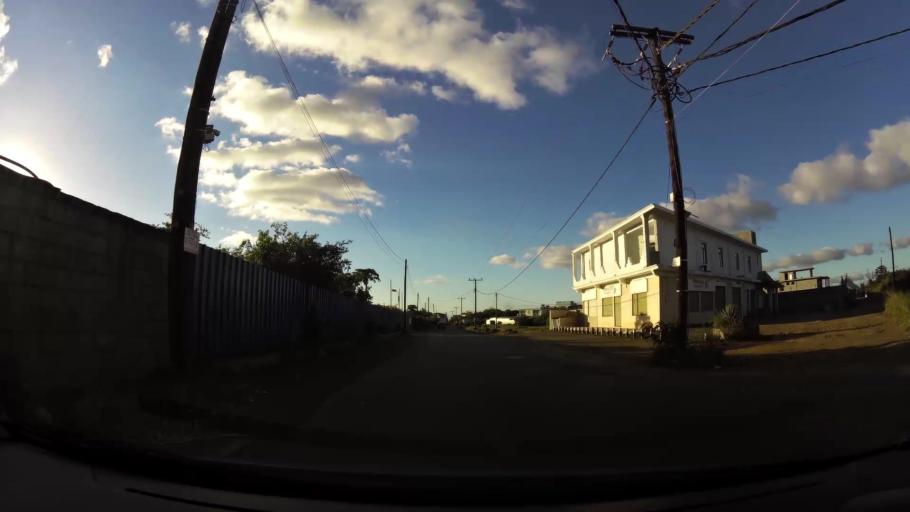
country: MU
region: Plaines Wilhems
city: Quatre Bornes
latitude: -20.2584
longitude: 57.4617
